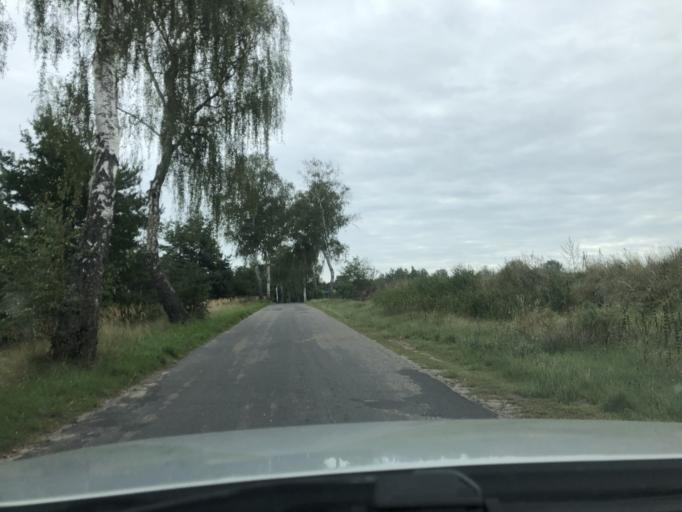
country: PL
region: Greater Poland Voivodeship
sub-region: Powiat pilski
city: Szydlowo
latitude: 53.2681
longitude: 16.6139
